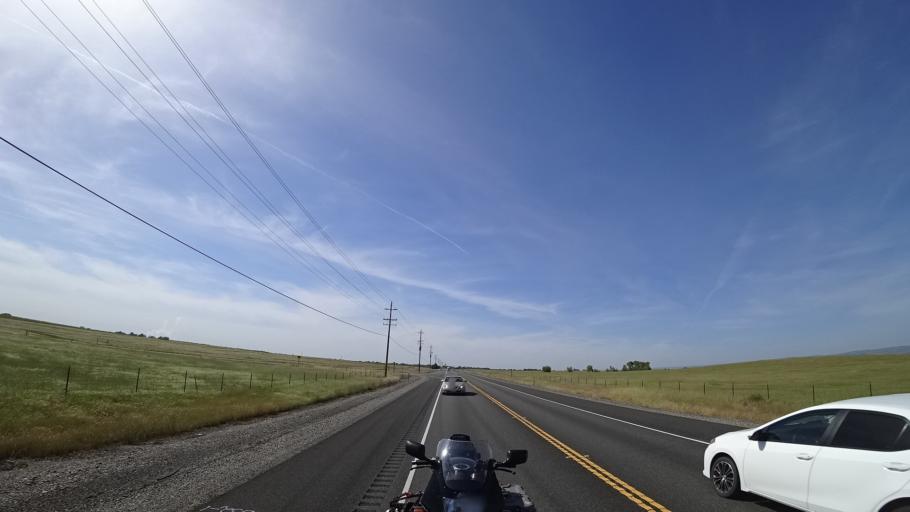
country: US
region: California
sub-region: Glenn County
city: Hamilton City
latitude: 39.8592
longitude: -121.9559
